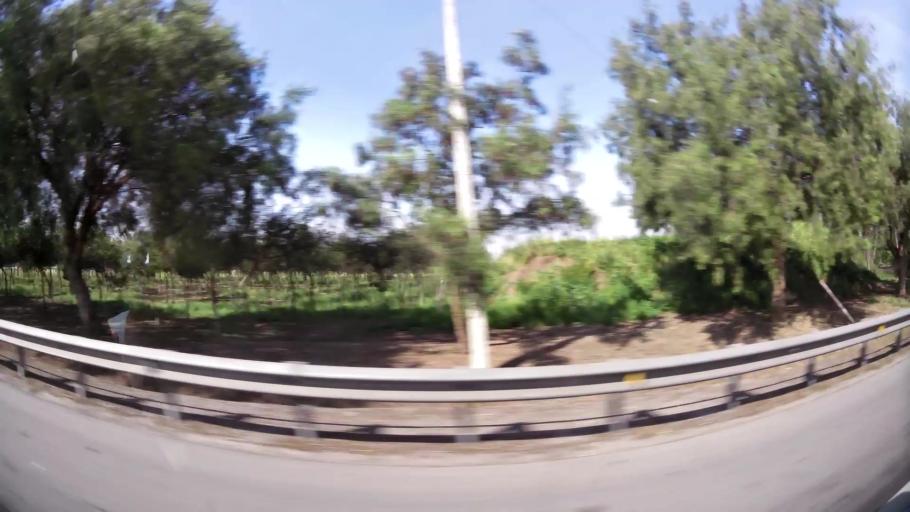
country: CL
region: Santiago Metropolitan
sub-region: Provincia de Santiago
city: Lo Prado
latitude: -33.4129
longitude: -70.7685
